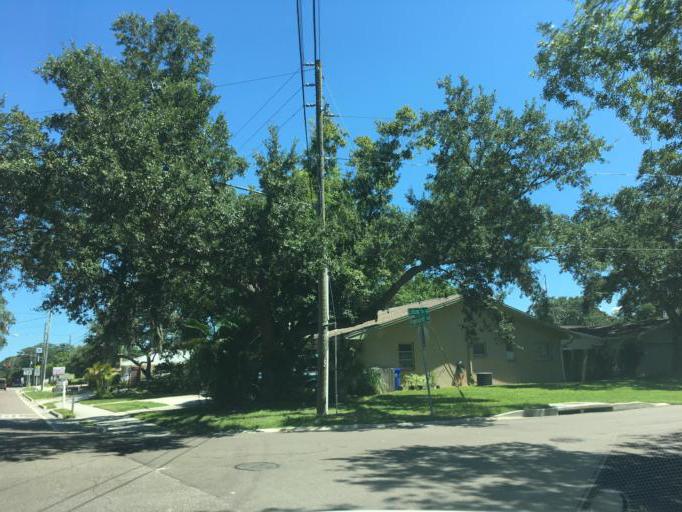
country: US
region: Florida
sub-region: Pinellas County
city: Dunedin
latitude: 28.0214
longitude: -82.7717
